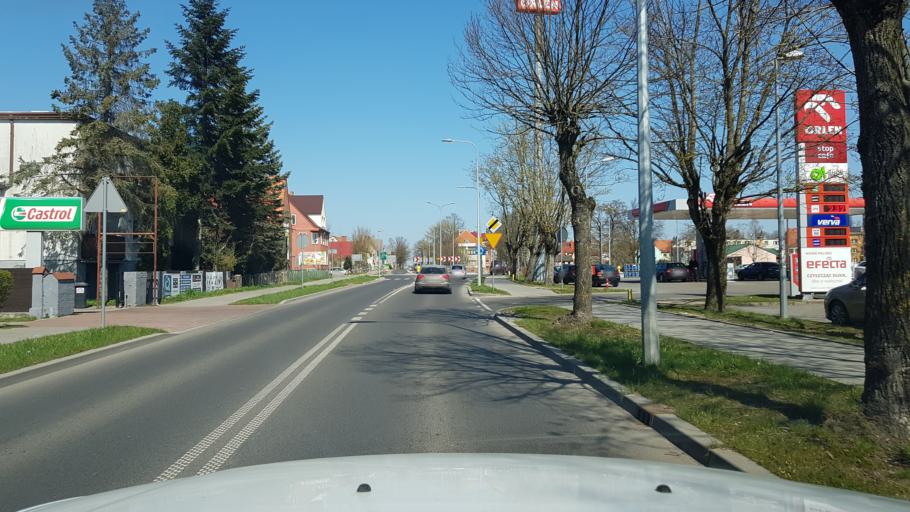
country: PL
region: West Pomeranian Voivodeship
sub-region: Powiat slawienski
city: Slawno
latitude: 54.3627
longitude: 16.6741
